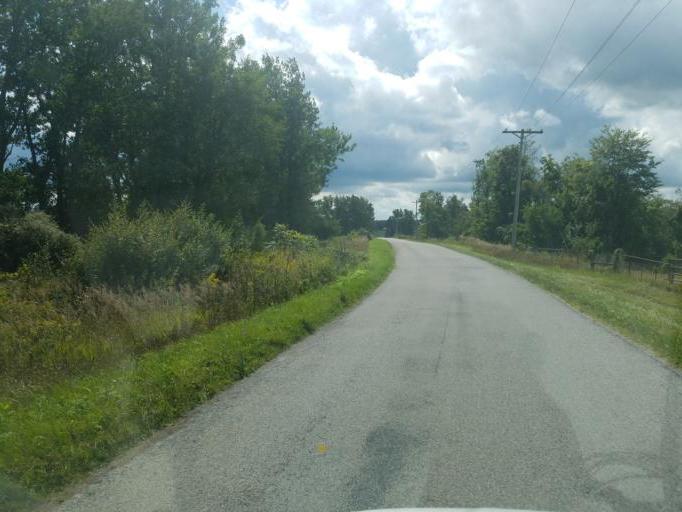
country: US
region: Ohio
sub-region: Huron County
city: Willard
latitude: 41.1146
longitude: -82.6286
